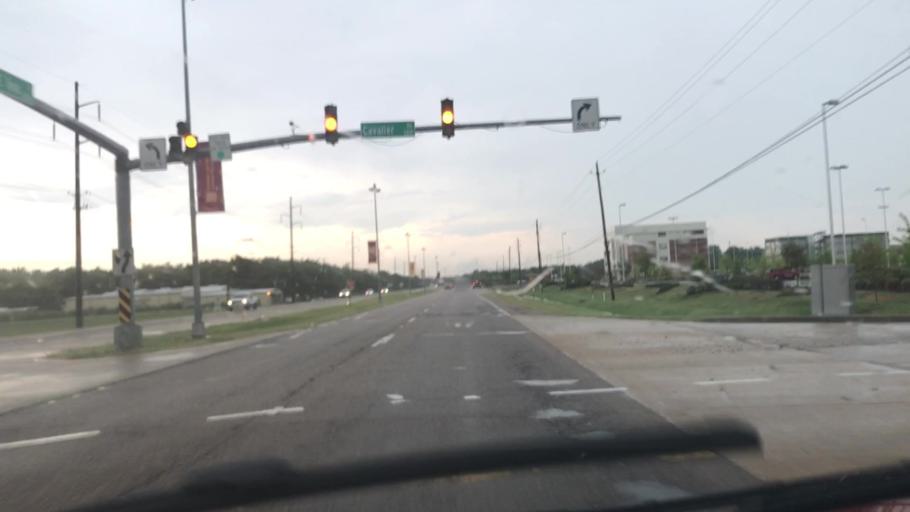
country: US
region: Louisiana
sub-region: Bossier Parish
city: Red Chute
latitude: 32.5410
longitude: -93.6486
